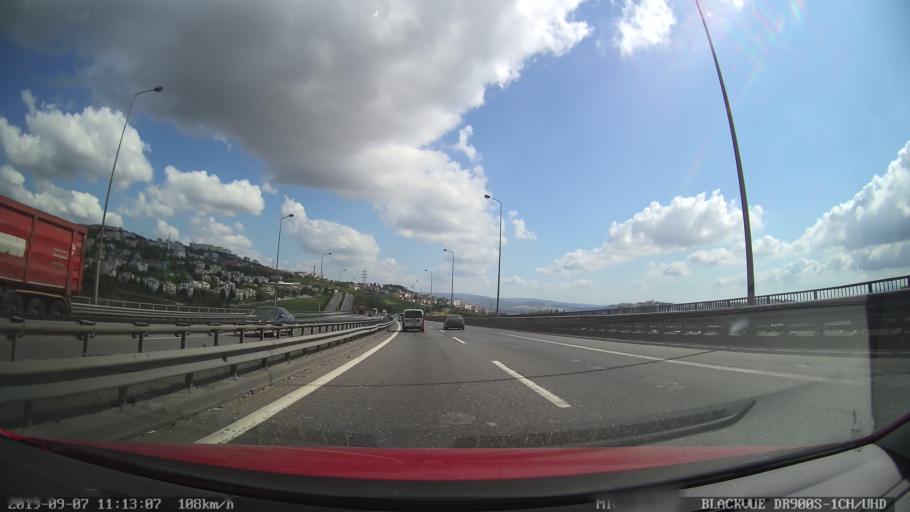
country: TR
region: Kocaeli
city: Izmit
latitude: 40.7818
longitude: 29.9414
